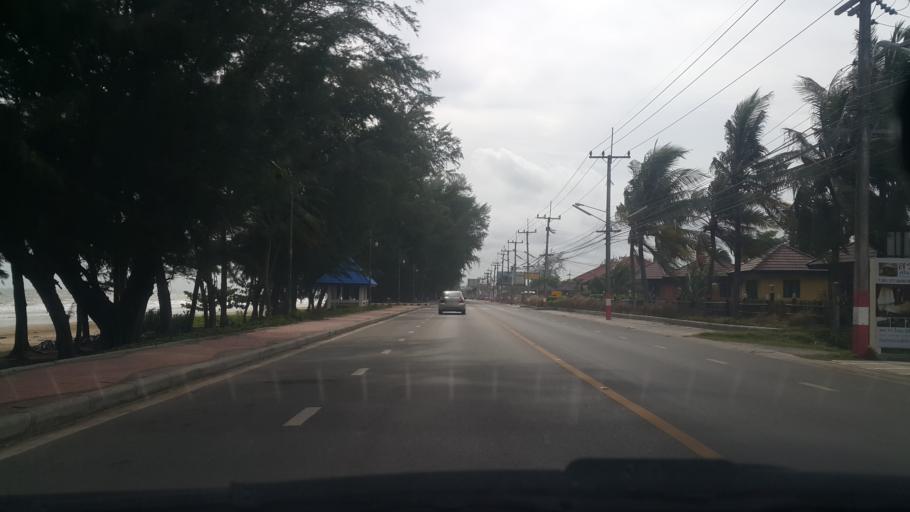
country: TH
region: Rayong
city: Rayong
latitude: 12.6243
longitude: 101.3592
